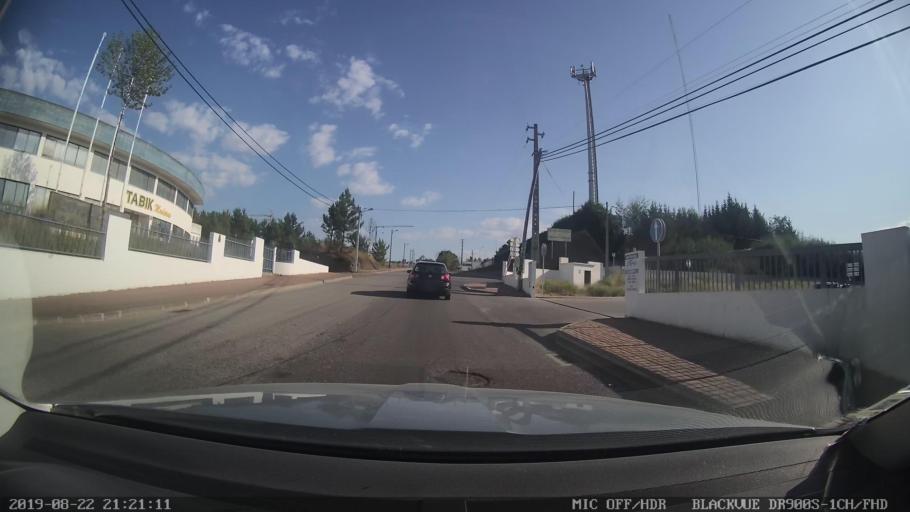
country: PT
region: Castelo Branco
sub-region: Serta
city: Serta
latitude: 39.8168
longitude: -8.1088
